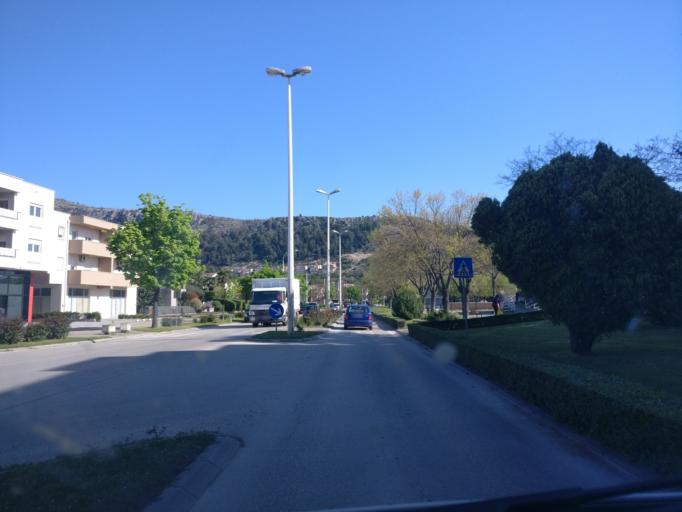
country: BA
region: Federation of Bosnia and Herzegovina
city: Capljina
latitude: 43.1111
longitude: 17.6996
